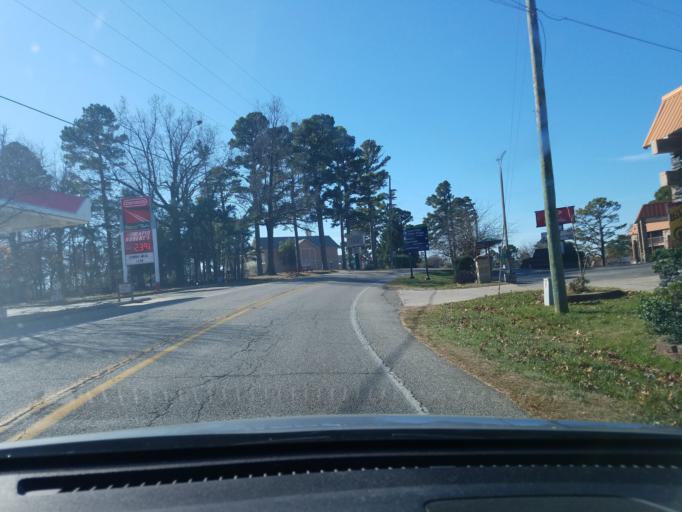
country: US
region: Arkansas
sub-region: Carroll County
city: Eureka Springs
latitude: 36.3882
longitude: -93.7338
